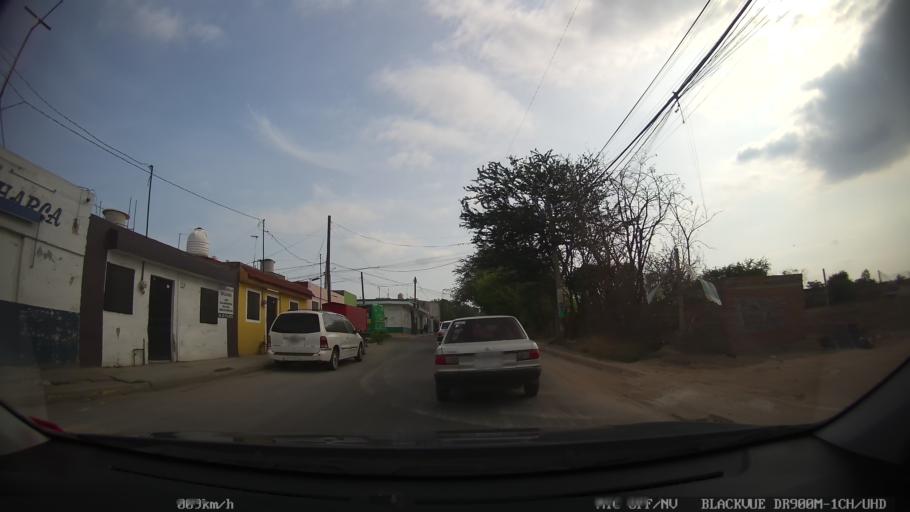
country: MX
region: Jalisco
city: Tonala
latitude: 20.6263
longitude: -103.2361
